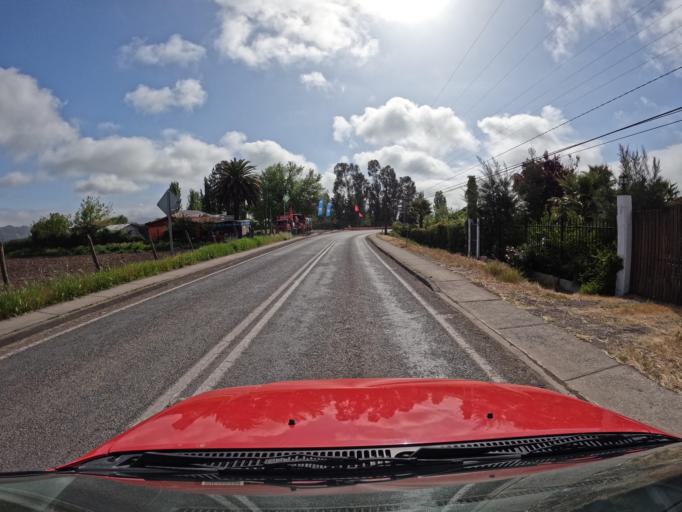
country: CL
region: Maule
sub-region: Provincia de Curico
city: Teno
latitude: -34.8608
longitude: -71.1952
